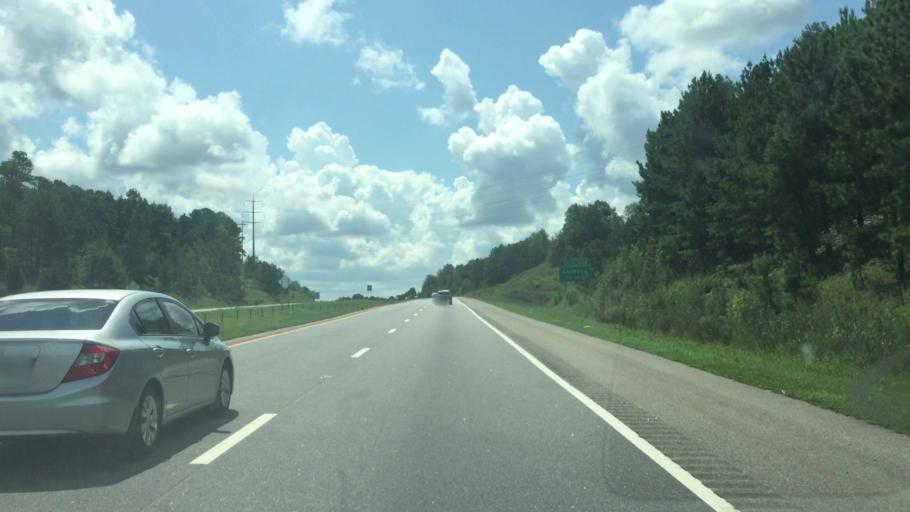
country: US
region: North Carolina
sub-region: Richmond County
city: Cordova
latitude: 34.9402
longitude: -79.8429
